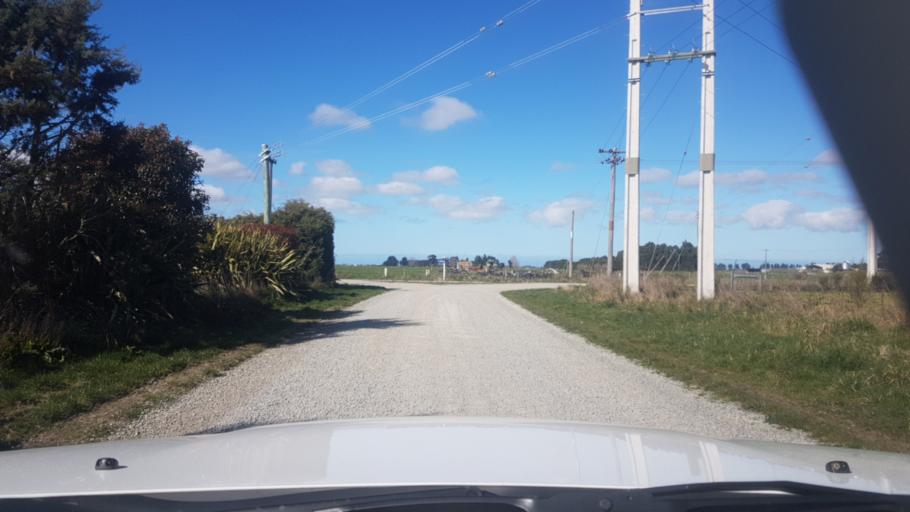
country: NZ
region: Canterbury
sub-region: Timaru District
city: Pleasant Point
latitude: -44.0992
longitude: 171.3898
